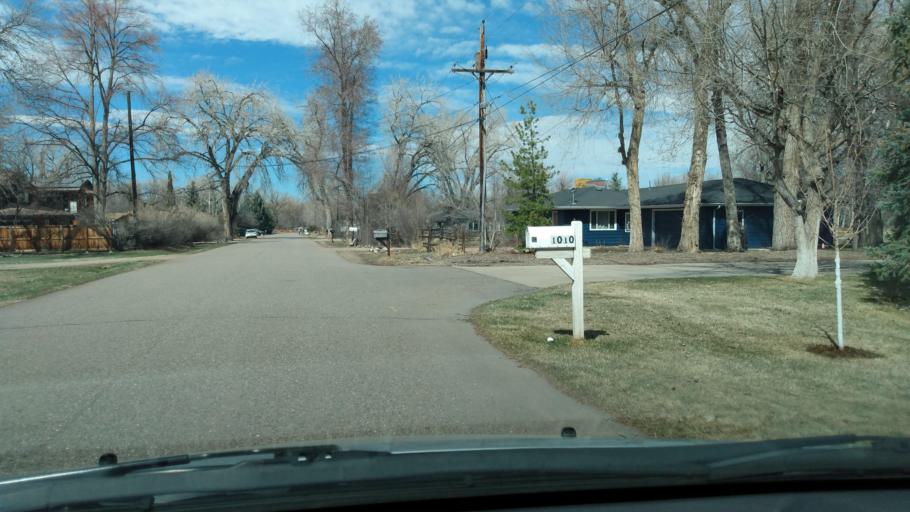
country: US
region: Colorado
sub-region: Boulder County
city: Boulder
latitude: 40.0051
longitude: -105.2150
